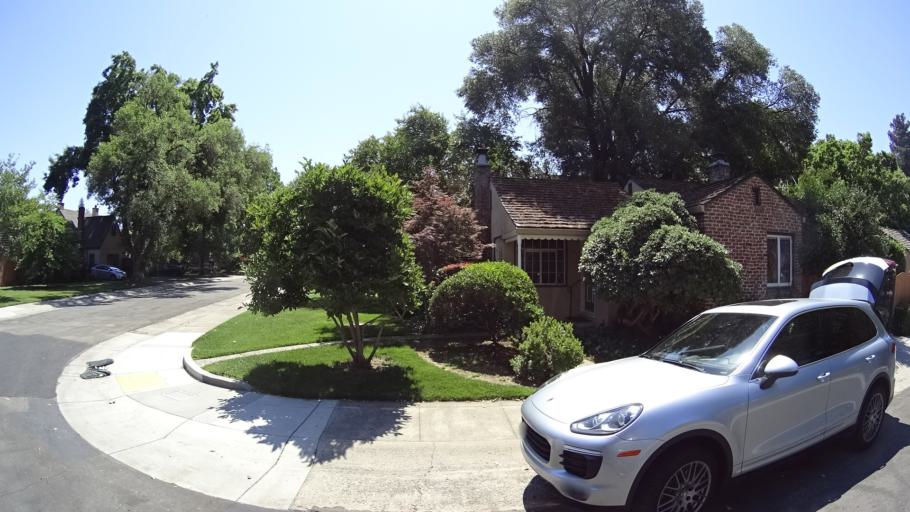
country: US
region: California
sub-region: Sacramento County
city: Sacramento
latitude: 38.5532
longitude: -121.4957
